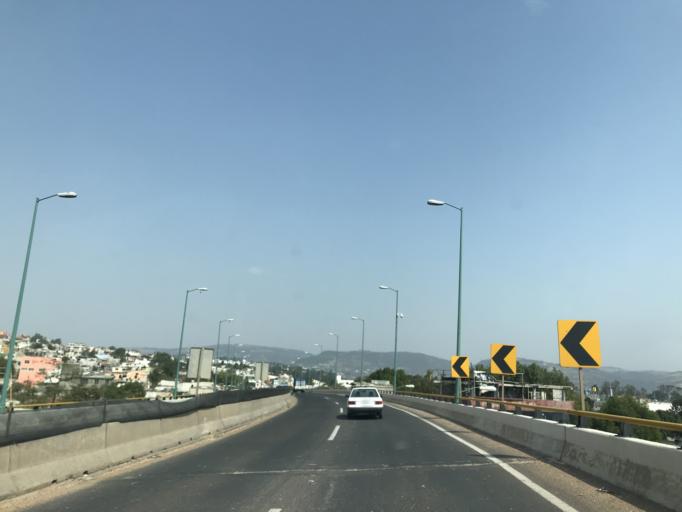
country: MX
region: Tlaxcala
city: Tlaxcala de Xicohtencatl
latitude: 19.3115
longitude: -98.2011
